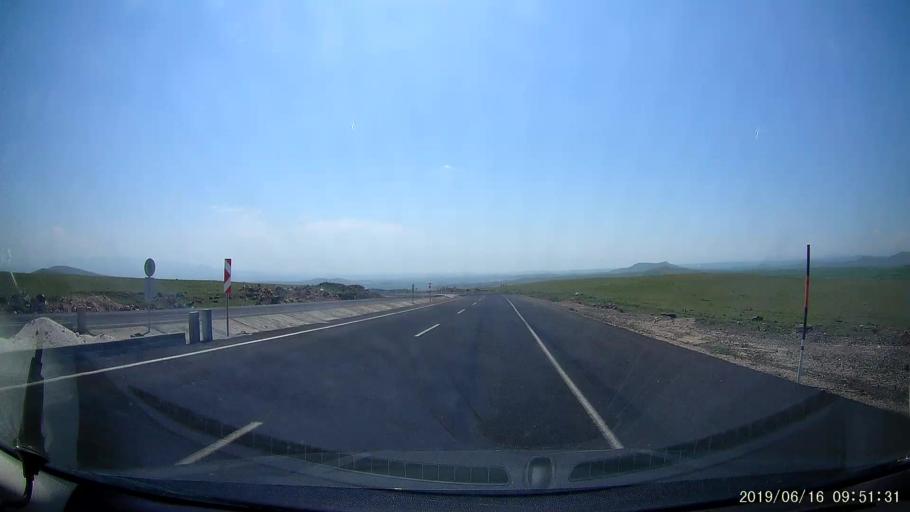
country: TR
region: Kars
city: Digor
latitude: 40.3911
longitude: 43.3681
